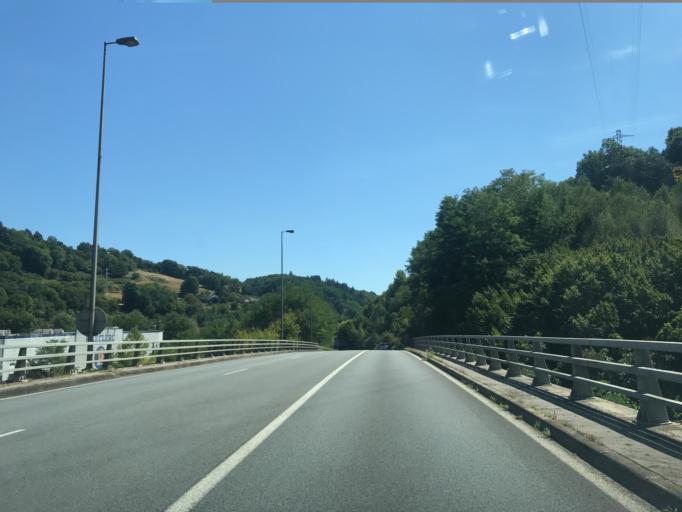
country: FR
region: Limousin
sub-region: Departement de la Correze
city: Tulle
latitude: 45.2520
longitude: 1.7594
